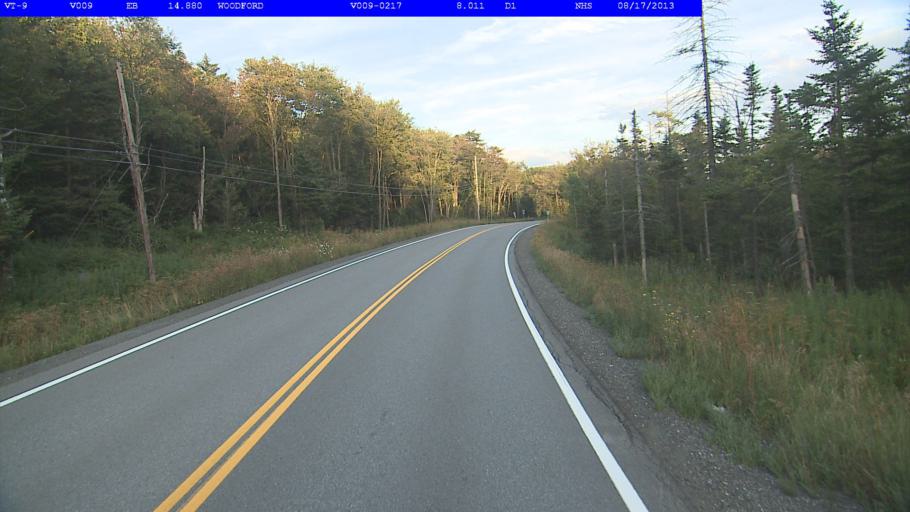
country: US
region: Vermont
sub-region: Bennington County
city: Bennington
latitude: 42.8947
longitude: -73.0386
